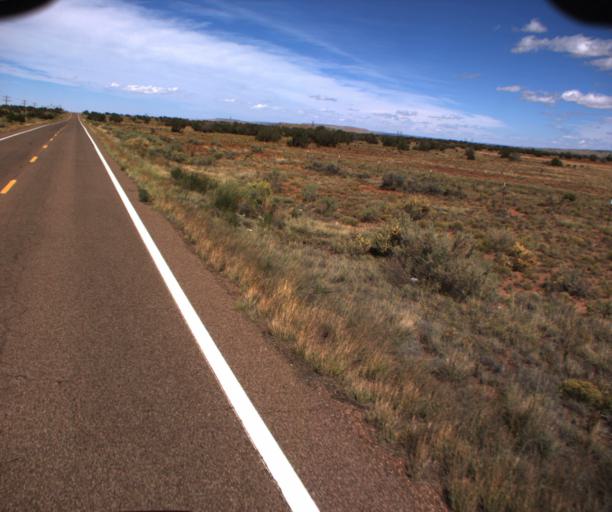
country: US
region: Arizona
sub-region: Apache County
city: Saint Johns
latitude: 34.5196
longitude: -109.6206
